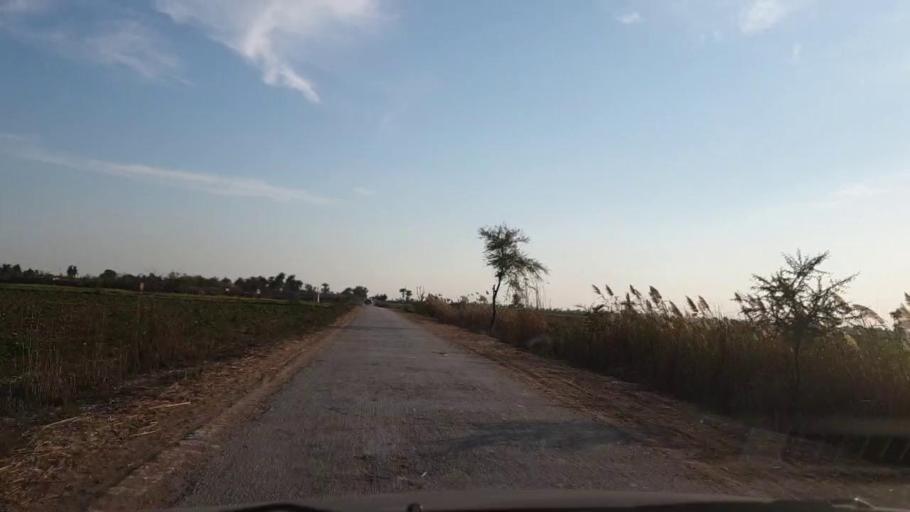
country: PK
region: Sindh
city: Khadro
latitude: 26.1748
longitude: 68.7529
